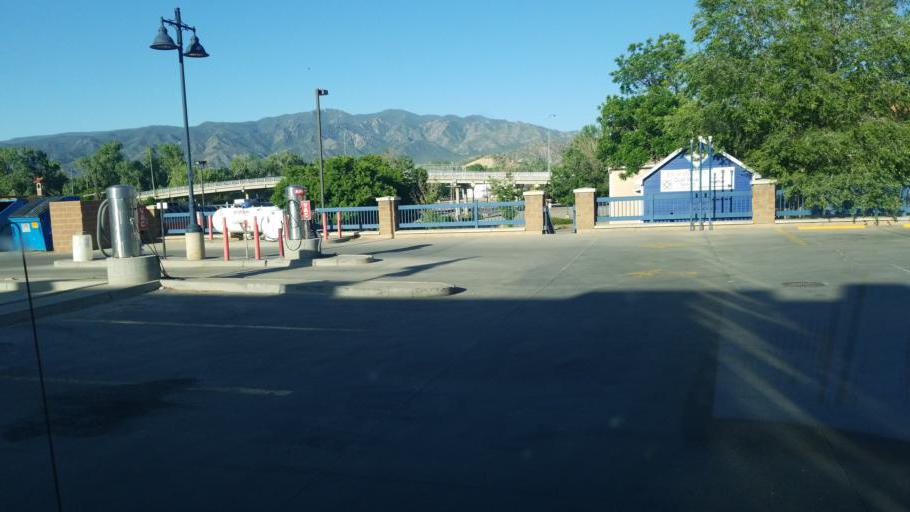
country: US
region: Colorado
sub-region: Fremont County
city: Canon City
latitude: 38.4390
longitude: -105.2403
